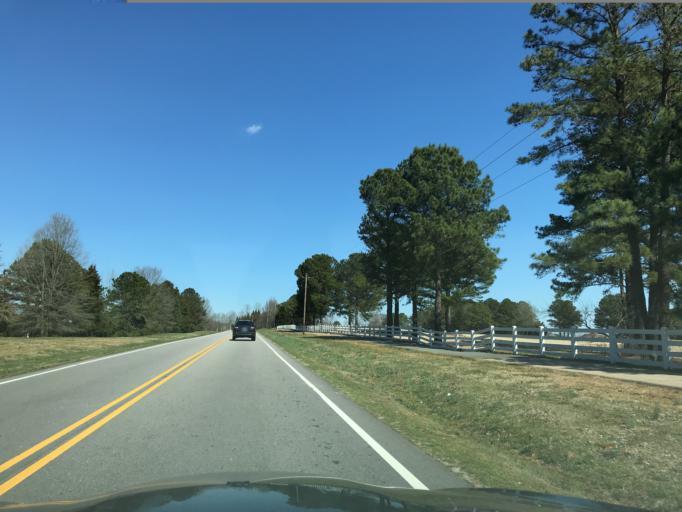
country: US
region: North Carolina
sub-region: Wake County
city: Wake Forest
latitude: 35.9579
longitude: -78.5649
